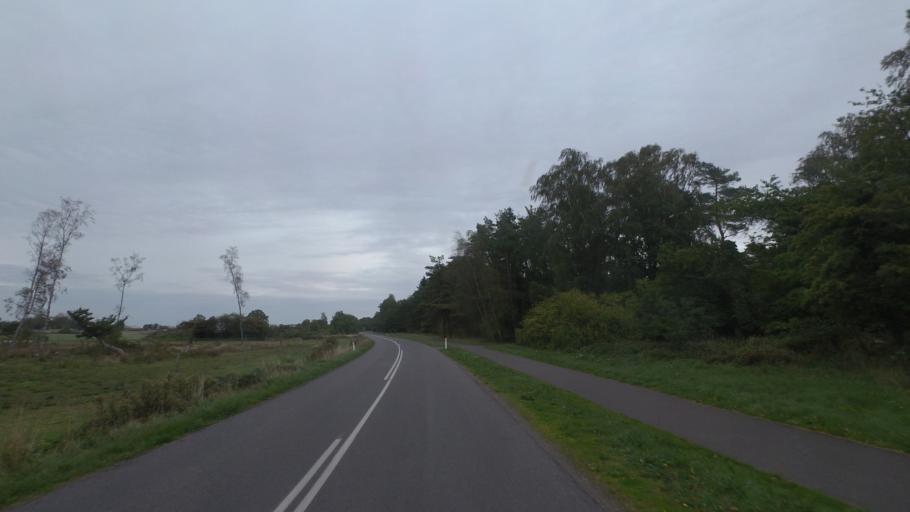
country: DK
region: Capital Region
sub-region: Bornholm Kommune
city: Nexo
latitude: 55.0017
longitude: 15.0747
